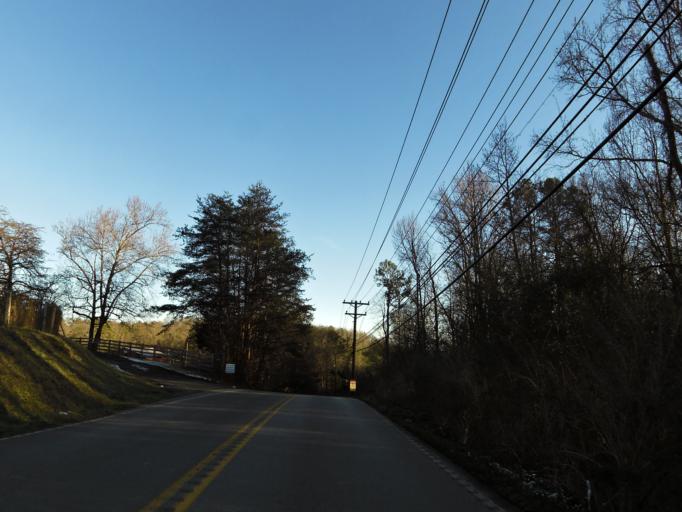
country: US
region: Tennessee
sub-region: Knox County
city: Farragut
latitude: 35.8854
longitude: -84.1309
